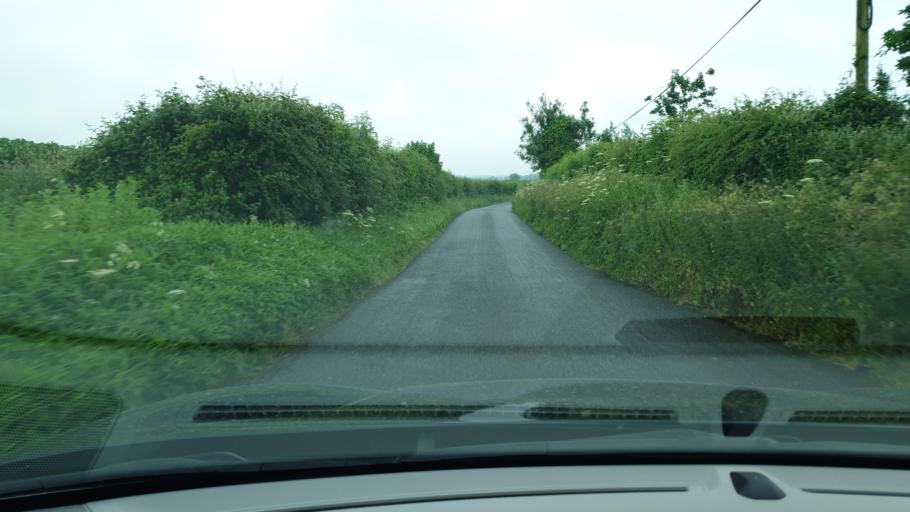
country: IE
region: Leinster
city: Hartstown
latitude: 53.4438
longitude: -6.4291
